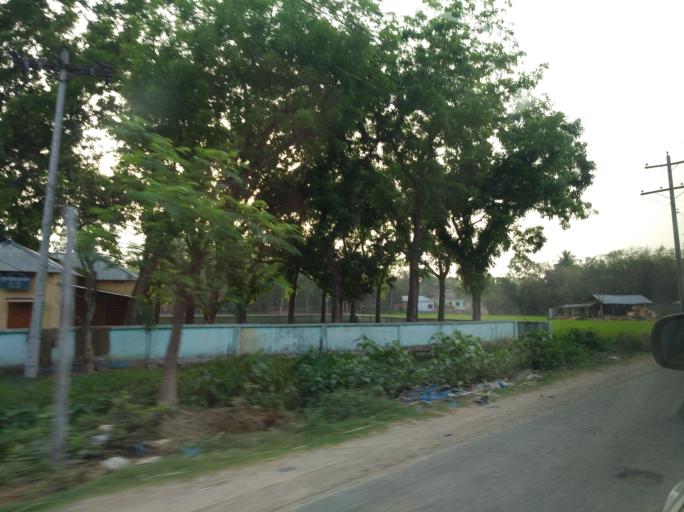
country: BD
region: Rajshahi
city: Bogra
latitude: 24.7042
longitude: 89.3980
